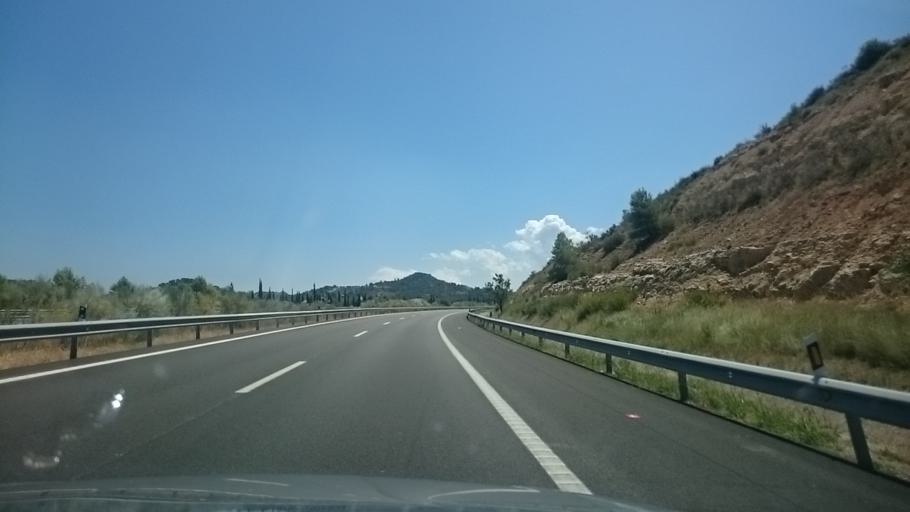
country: ES
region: Catalonia
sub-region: Provincia de Lleida
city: Vinaixa
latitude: 41.4437
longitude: 0.9155
